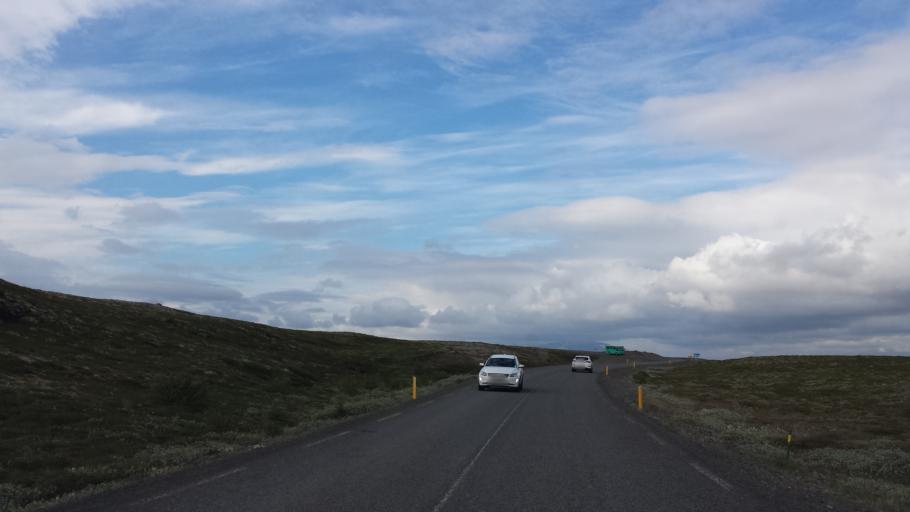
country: IS
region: South
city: Vestmannaeyjar
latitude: 64.3185
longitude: -20.1385
